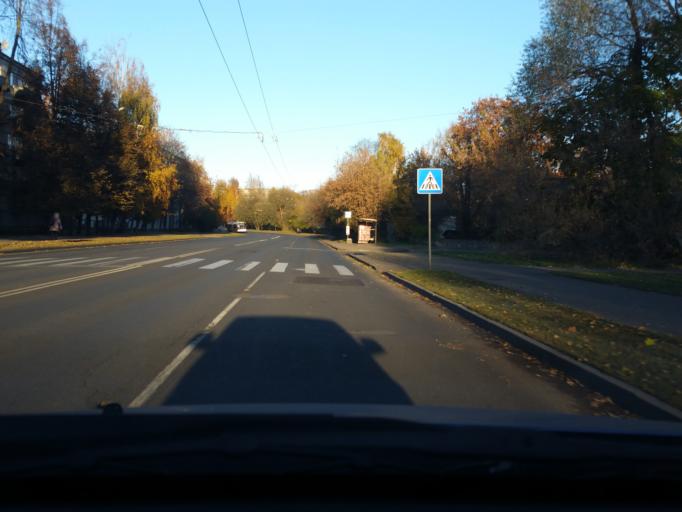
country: LV
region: Riga
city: Jaunciems
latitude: 56.9620
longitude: 24.1912
